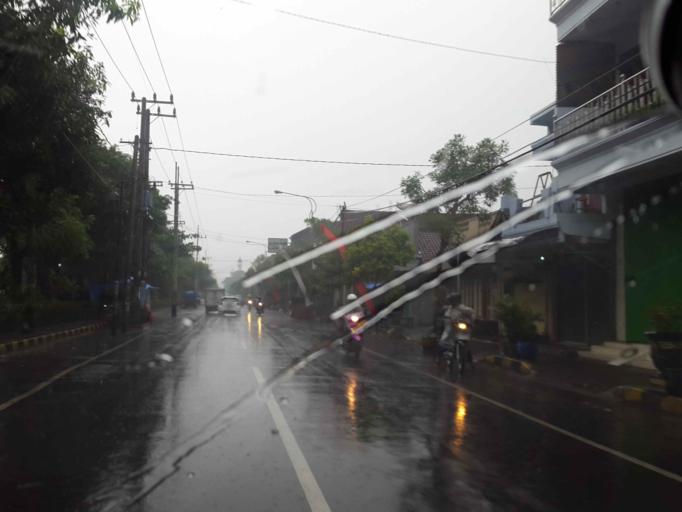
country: ID
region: East Java
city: Penarukan
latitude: -8.1356
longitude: 112.5784
